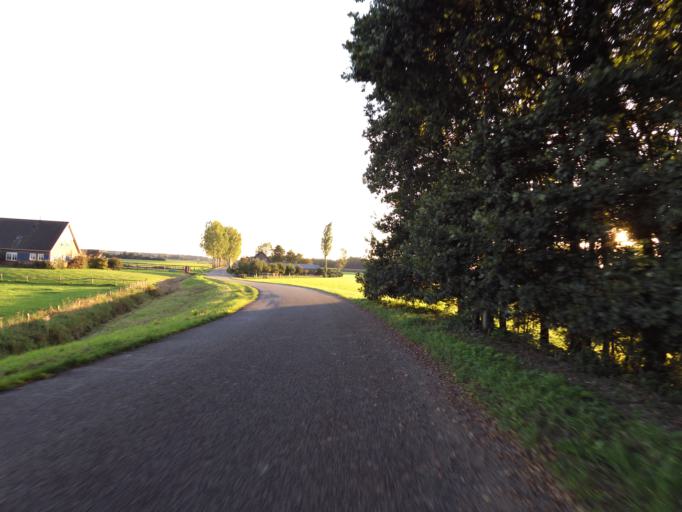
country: NL
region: Gelderland
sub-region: Gemeente Doesburg
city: Doesburg
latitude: 51.9277
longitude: 6.1605
